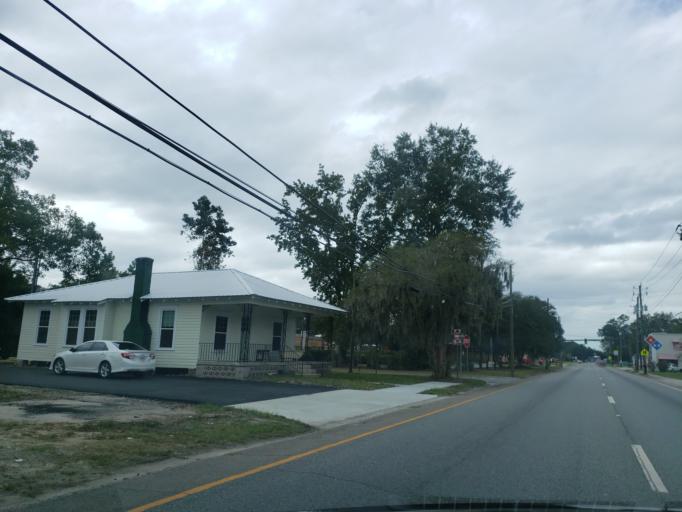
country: US
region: Georgia
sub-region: Chatham County
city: Pooler
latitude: 32.1156
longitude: -81.2473
